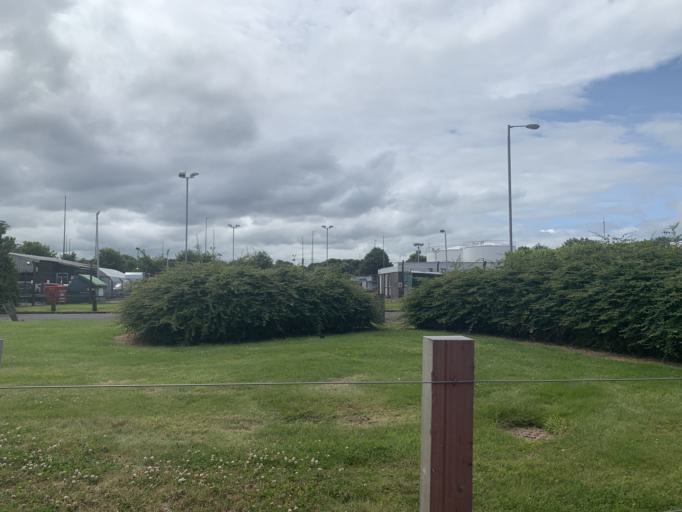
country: GB
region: Scotland
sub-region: Renfrewshire
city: Inchinnan
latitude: 55.8629
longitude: -4.4372
